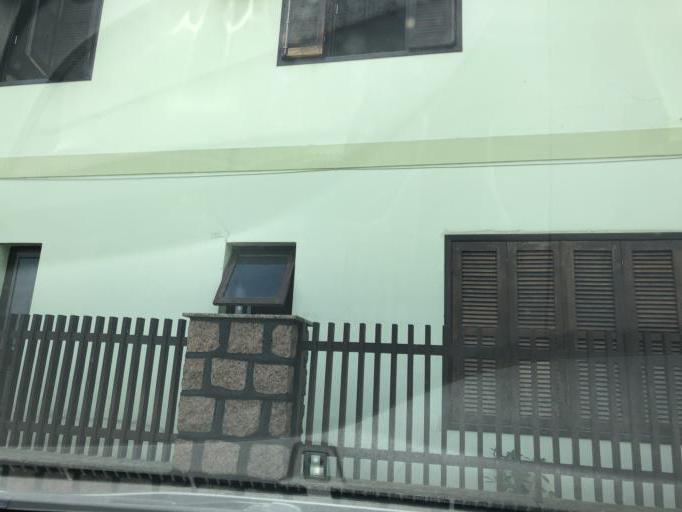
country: BR
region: Santa Catarina
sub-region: Jaragua Do Sul
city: Jaragua do Sul
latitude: -26.5182
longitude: -49.1317
